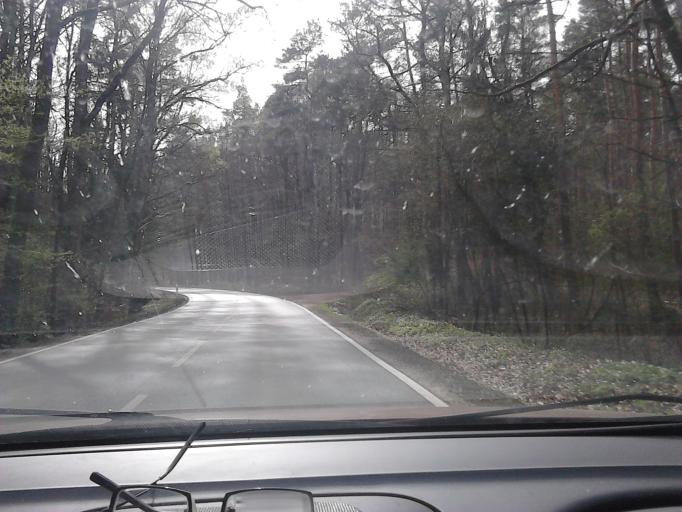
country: DE
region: Thuringia
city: Hellingen
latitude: 50.2697
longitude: 10.7033
